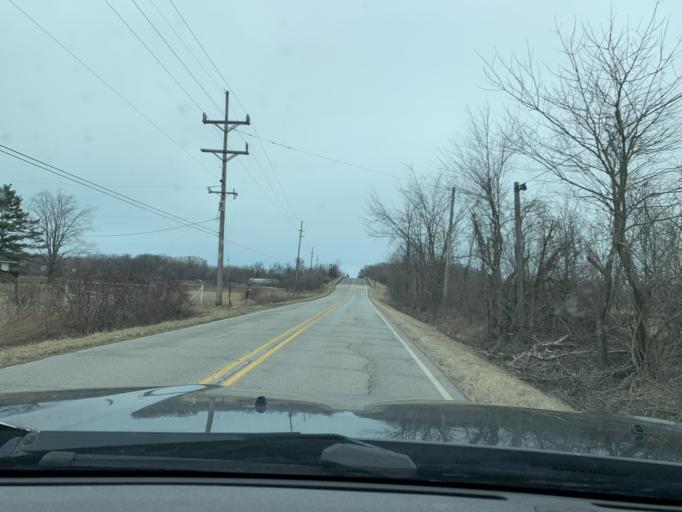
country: US
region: Indiana
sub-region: Porter County
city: Chesterton
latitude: 41.5750
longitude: -87.0666
